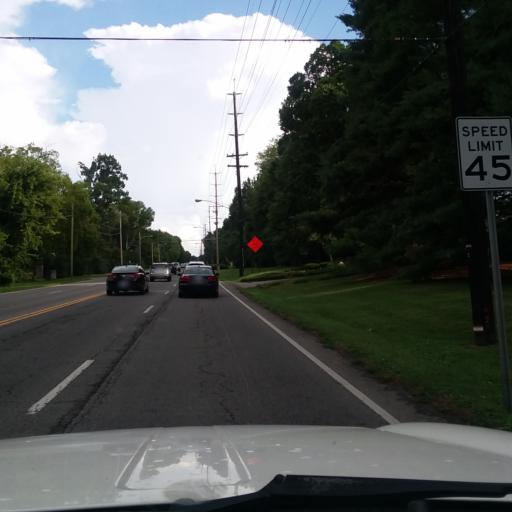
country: US
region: Tennessee
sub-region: Davidson County
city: Oak Hill
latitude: 36.0978
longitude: -86.7721
